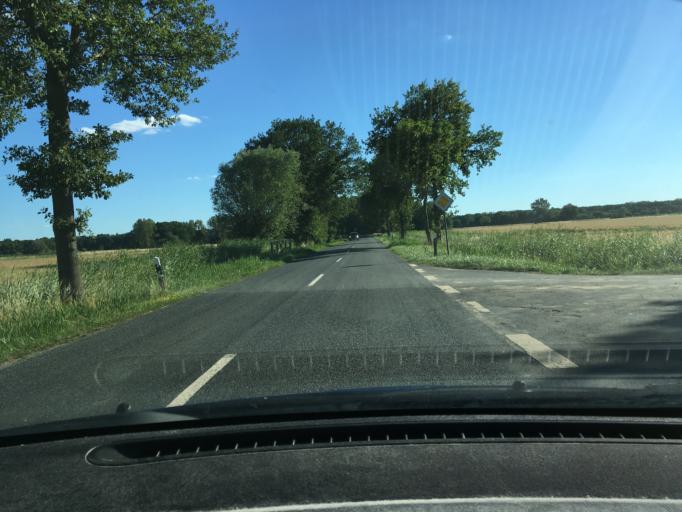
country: DE
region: Lower Saxony
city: Bleckede
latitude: 53.3295
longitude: 10.7064
